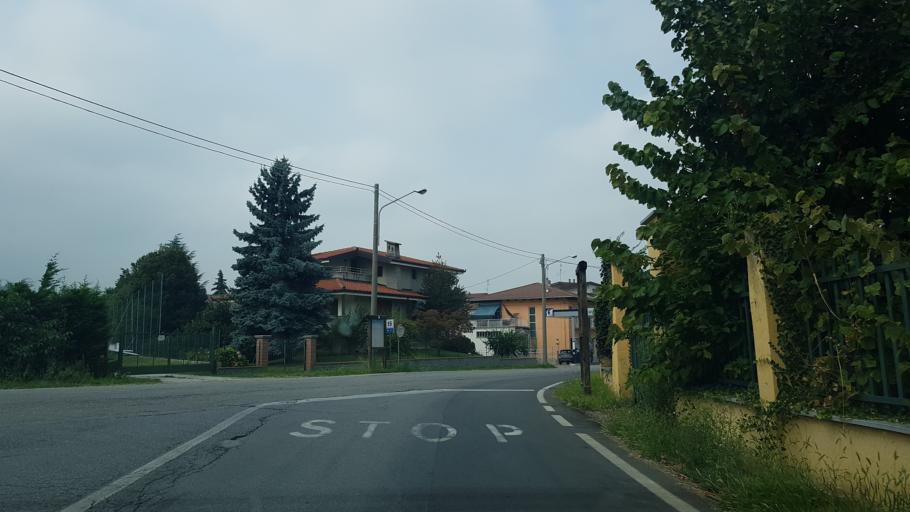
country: IT
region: Piedmont
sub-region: Provincia di Cuneo
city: Chiusa di Pesio
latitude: 44.3281
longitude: 7.6708
